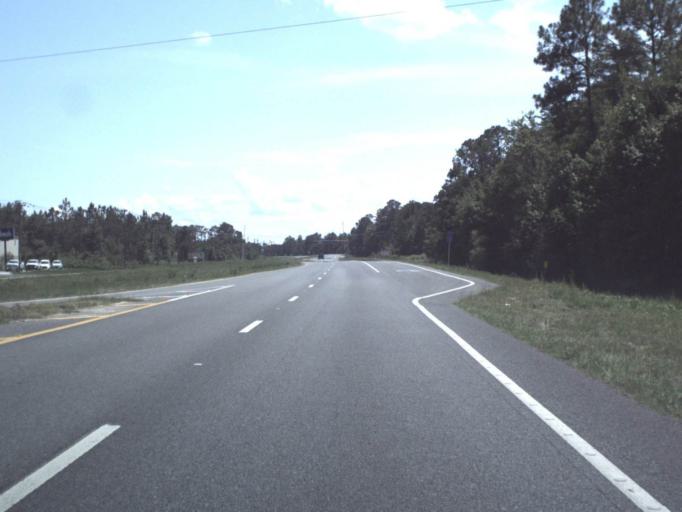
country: US
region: Florida
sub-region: Putnam County
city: Palatka
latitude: 29.6901
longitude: -81.6630
